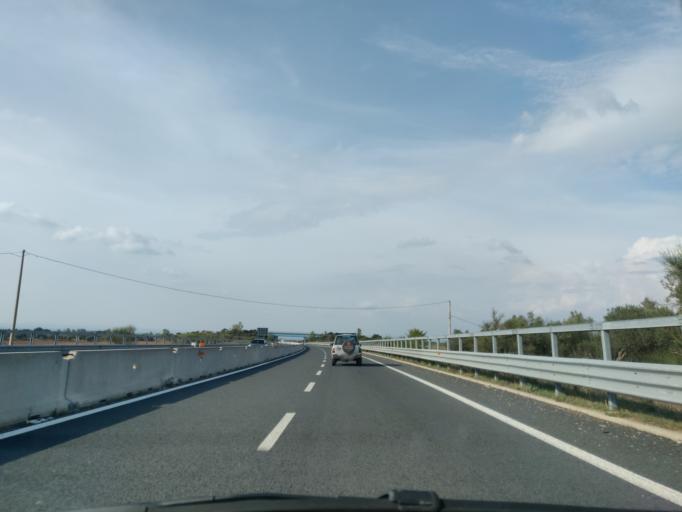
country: IT
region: Latium
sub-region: Provincia di Viterbo
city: Blera
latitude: 42.3128
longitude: 11.9919
